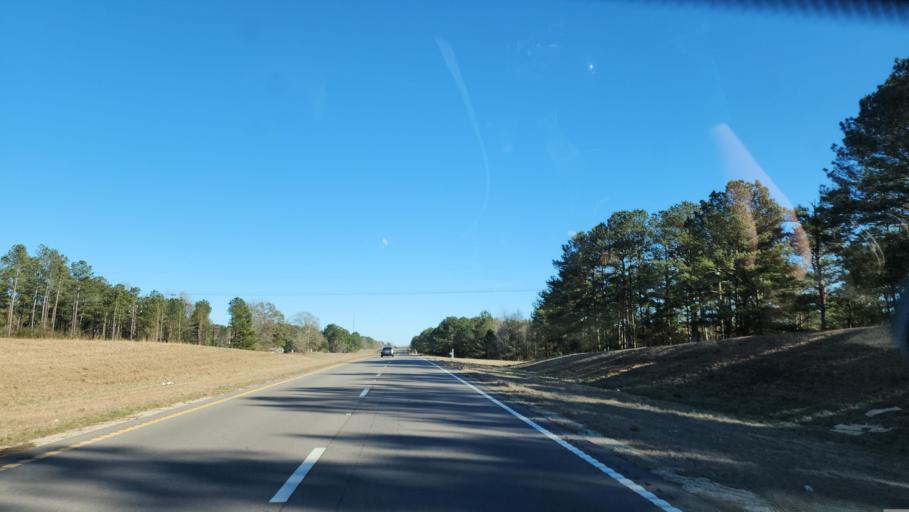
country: US
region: Mississippi
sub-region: Jones County
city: Sharon
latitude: 31.7064
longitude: -88.9384
